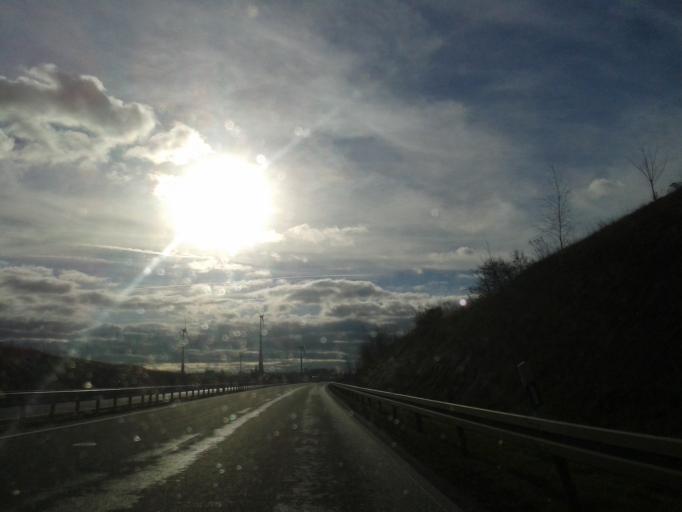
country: DE
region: Saxony
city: Lobau
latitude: 51.1421
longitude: 14.6541
